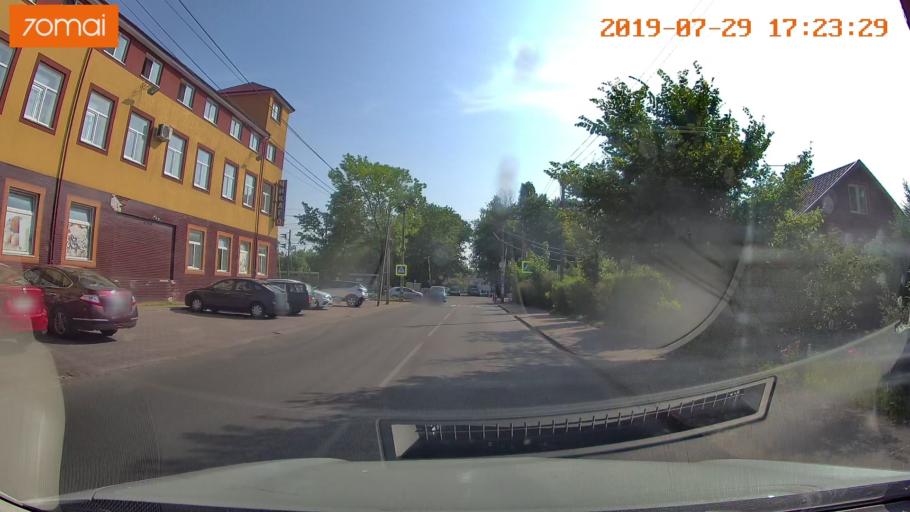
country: RU
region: Kaliningrad
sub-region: Gorod Kaliningrad
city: Kaliningrad
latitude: 54.7654
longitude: 20.4448
